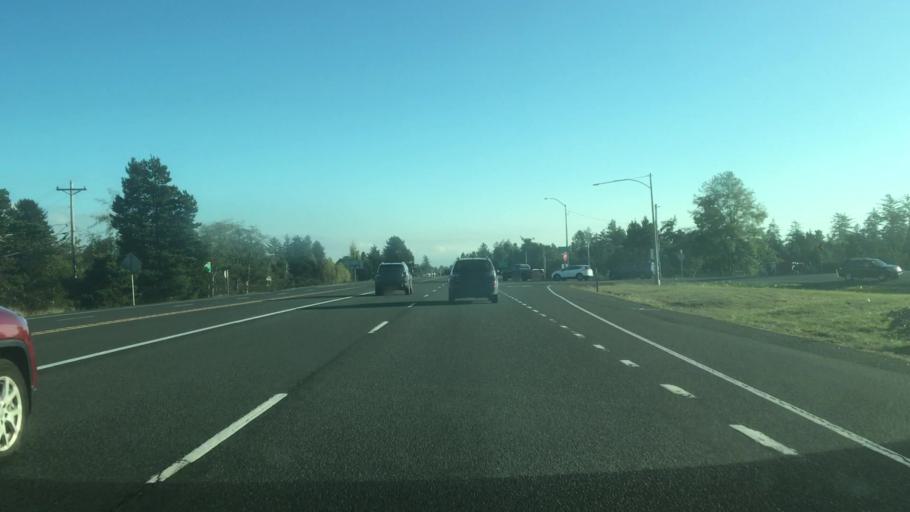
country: US
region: Oregon
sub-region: Clatsop County
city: Warrenton
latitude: 46.1293
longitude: -123.9286
